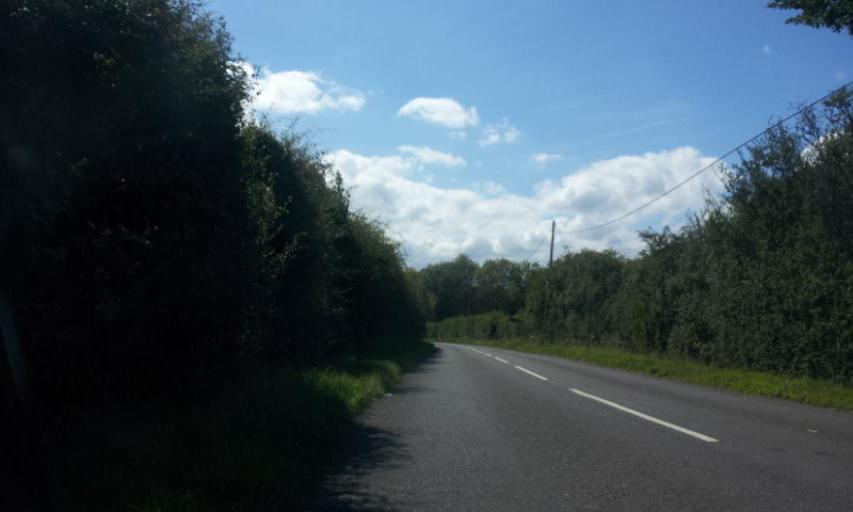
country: GB
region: England
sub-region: Kent
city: Marden
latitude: 51.1845
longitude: 0.4893
